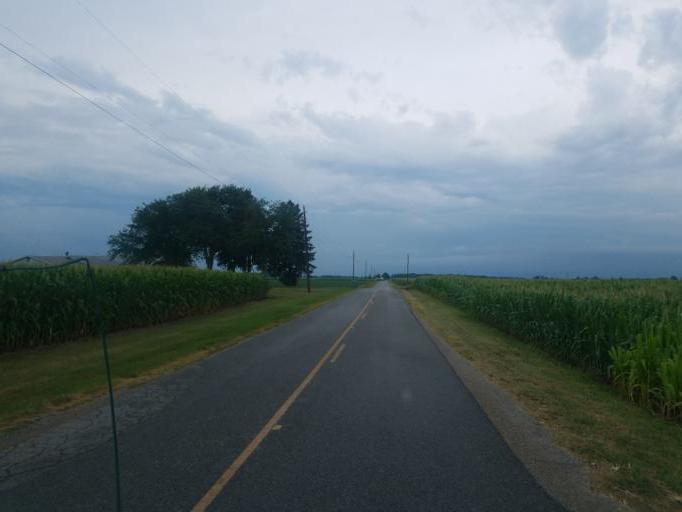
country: US
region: Ohio
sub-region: Paulding County
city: Antwerp
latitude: 41.2372
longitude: -84.7423
